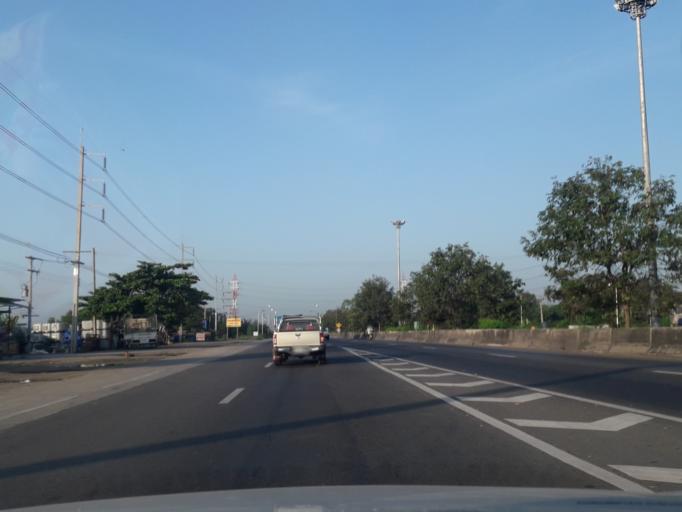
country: TH
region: Phra Nakhon Si Ayutthaya
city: Bang Pa-in
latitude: 14.1530
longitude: 100.5616
